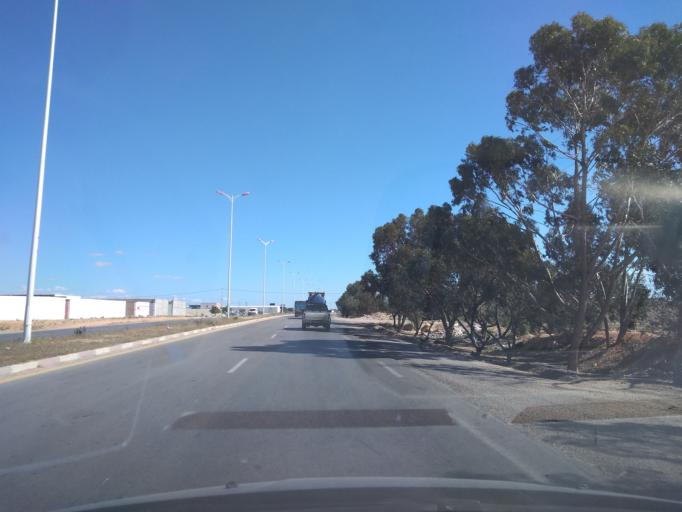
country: TN
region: Safaqis
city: Sfax
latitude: 34.8152
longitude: 10.6992
